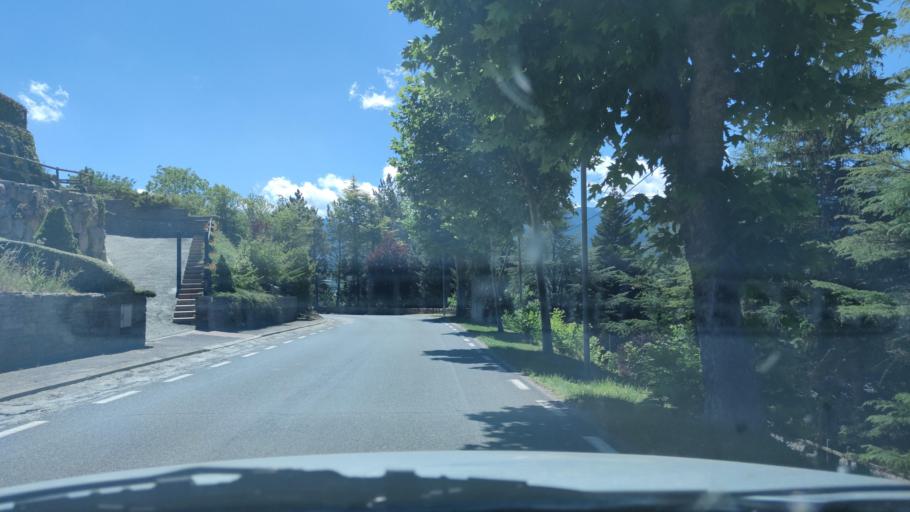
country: ES
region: Catalonia
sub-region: Provincia de Lleida
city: Bellver de Cerdanya
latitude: 42.3775
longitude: 1.7400
